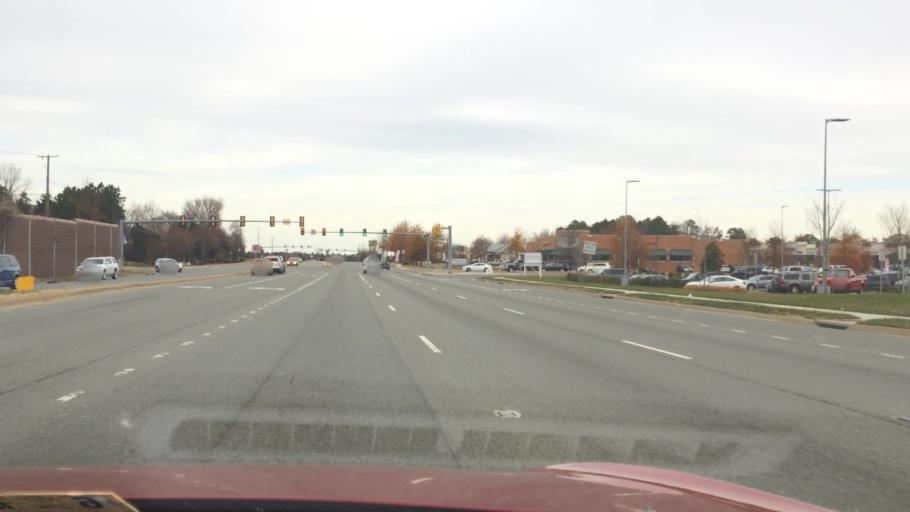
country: US
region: Virginia
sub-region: Henrico County
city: Glen Allen
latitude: 37.6650
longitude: -77.4604
